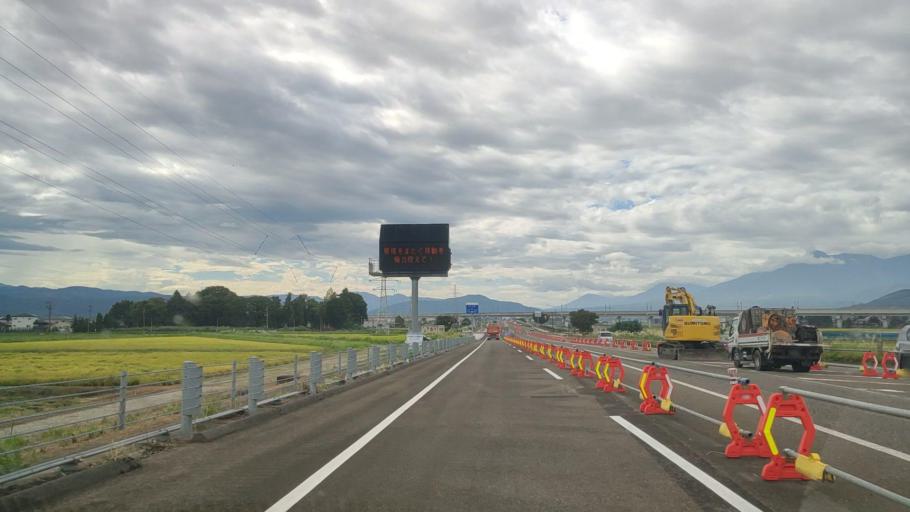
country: JP
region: Niigata
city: Joetsu
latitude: 37.0750
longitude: 138.2652
